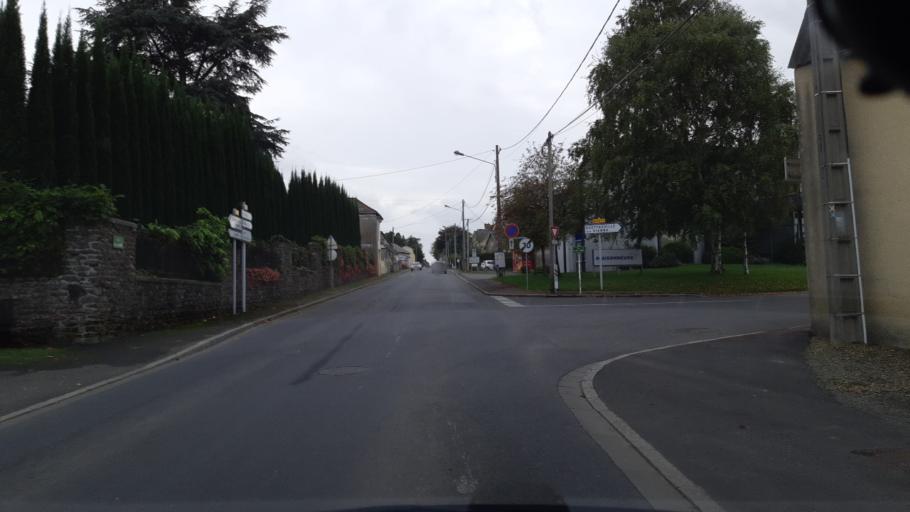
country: FR
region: Lower Normandy
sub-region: Departement de la Manche
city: Quettreville-sur-Sienne
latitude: 48.9204
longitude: -1.4283
